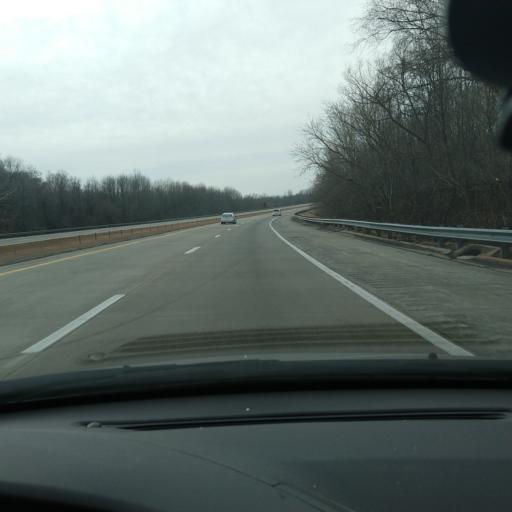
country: US
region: North Carolina
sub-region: Davidson County
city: Welcome
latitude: 35.8825
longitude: -80.2306
